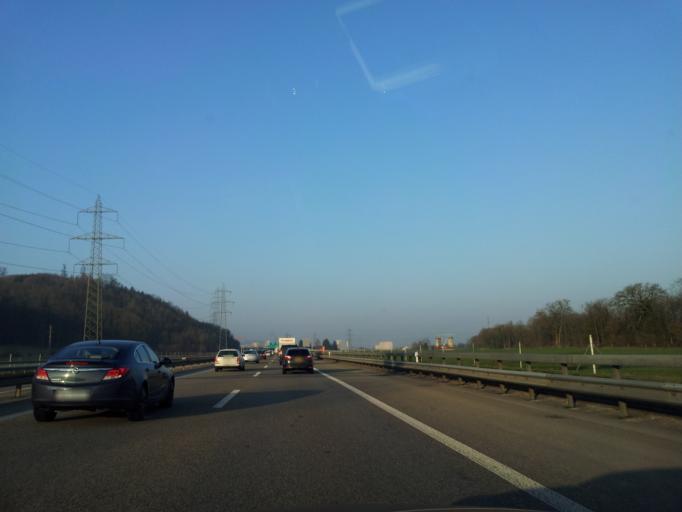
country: DE
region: Baden-Wuerttemberg
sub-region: Freiburg Region
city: Rheinfelden (Baden)
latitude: 47.5432
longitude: 7.7720
